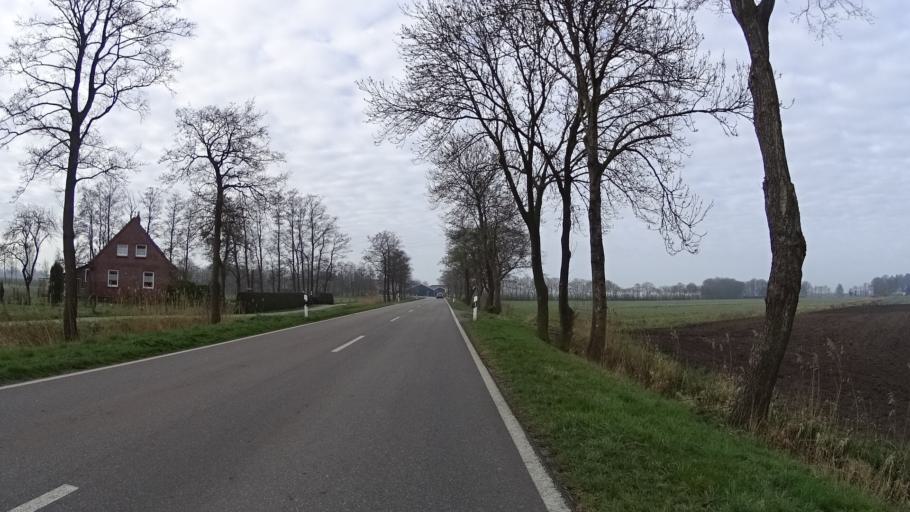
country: DE
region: Lower Saxony
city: Upgant-Schott
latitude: 53.4383
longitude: 7.3217
